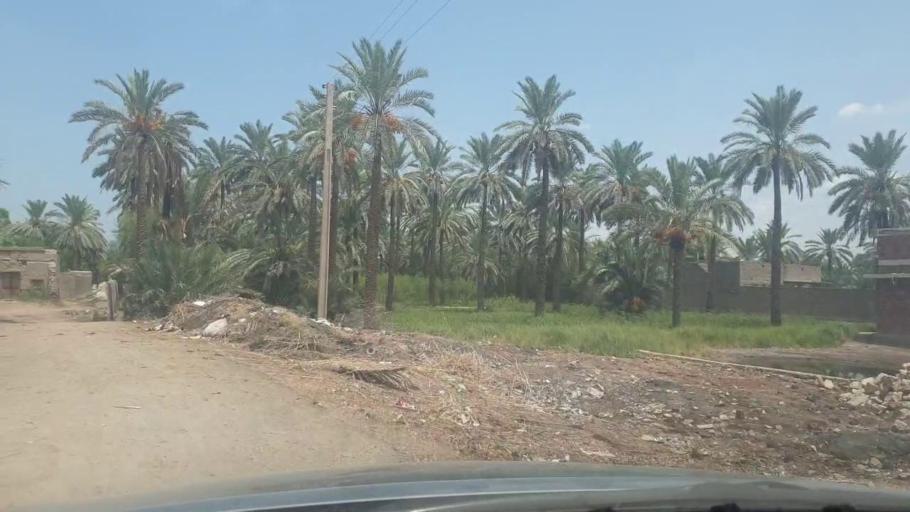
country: PK
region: Sindh
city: Kot Diji
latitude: 27.3976
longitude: 68.7706
